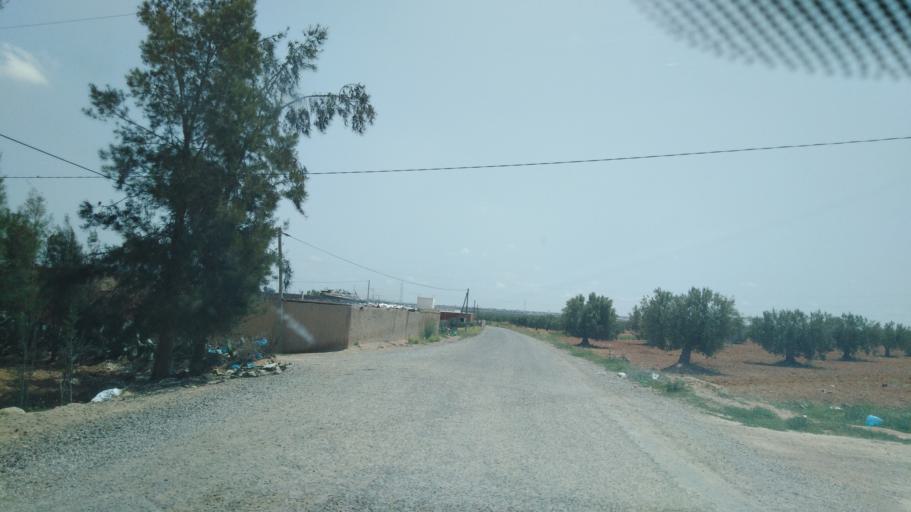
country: TN
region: Safaqis
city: Sfax
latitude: 34.7490
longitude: 10.5701
